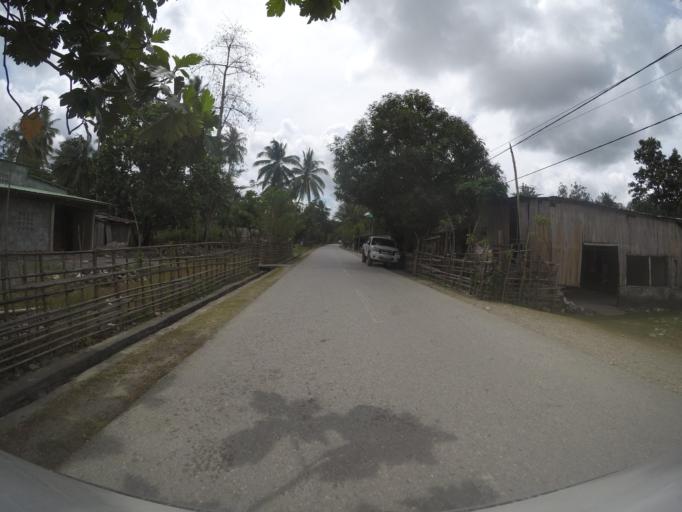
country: TL
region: Viqueque
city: Viqueque
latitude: -8.8533
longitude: 126.3641
